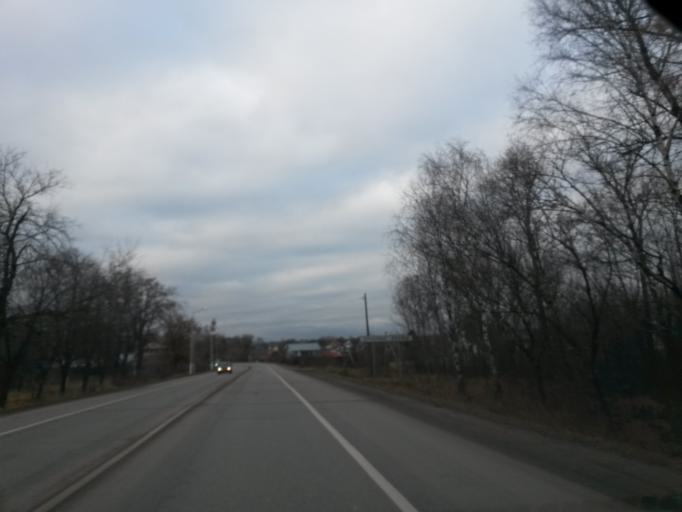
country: RU
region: Moskovskaya
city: Stolbovaya
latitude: 55.2134
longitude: 37.5060
